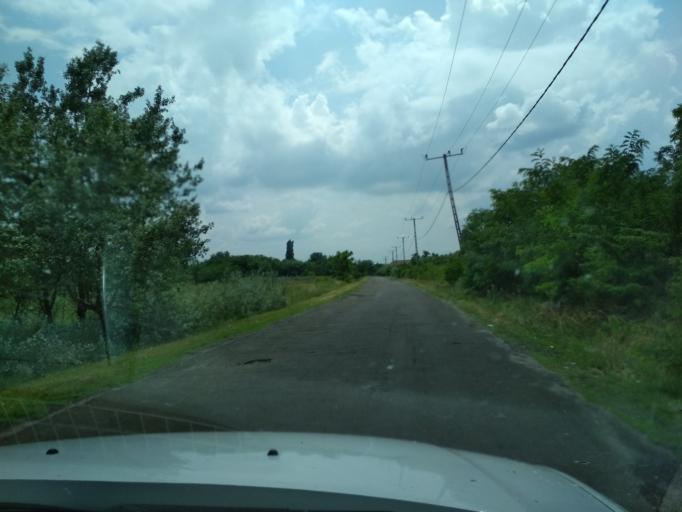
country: HU
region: Pest
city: Nagykata
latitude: 47.3779
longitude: 19.7573
